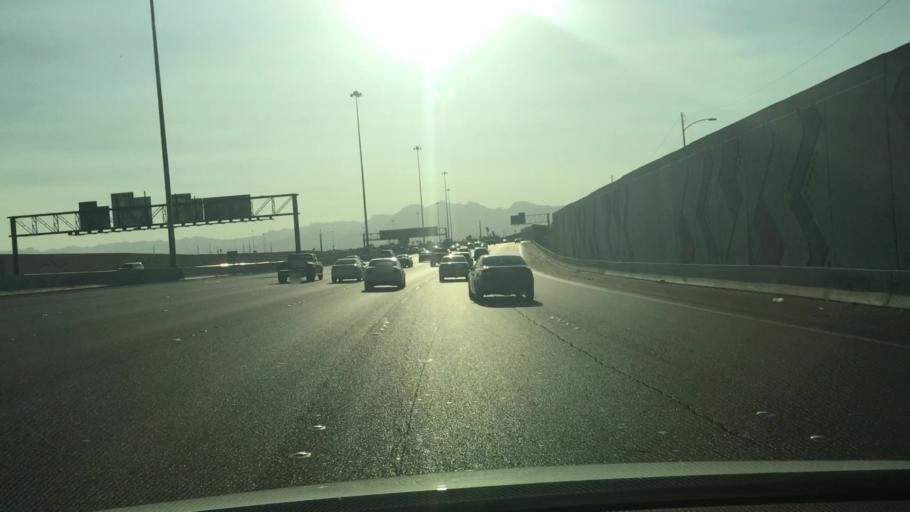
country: US
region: Nevada
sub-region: Clark County
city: Las Vegas
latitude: 36.1755
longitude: -115.1834
